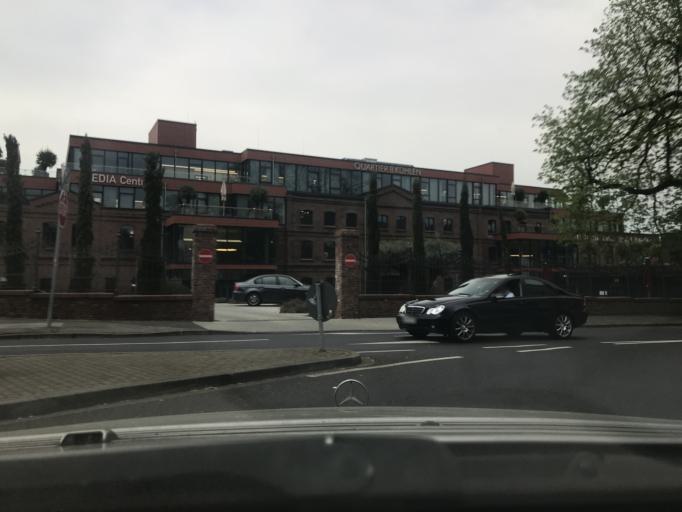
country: DE
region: North Rhine-Westphalia
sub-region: Regierungsbezirk Dusseldorf
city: Monchengladbach
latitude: 51.2041
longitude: 6.4413
